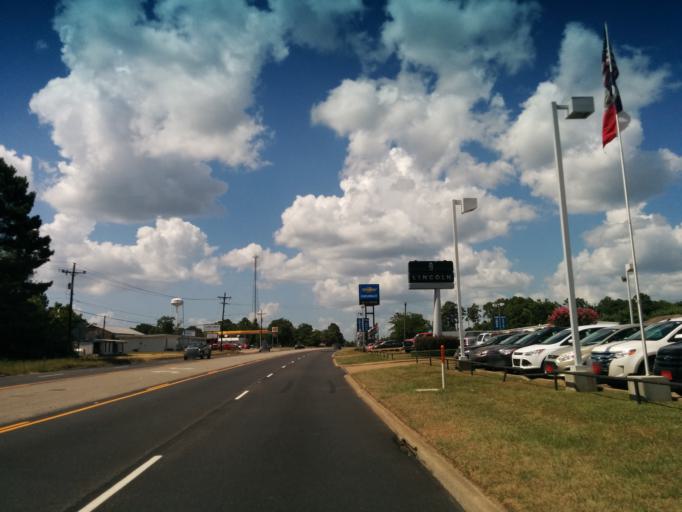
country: US
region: Texas
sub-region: Jasper County
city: Jasper
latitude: 30.9389
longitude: -93.9969
